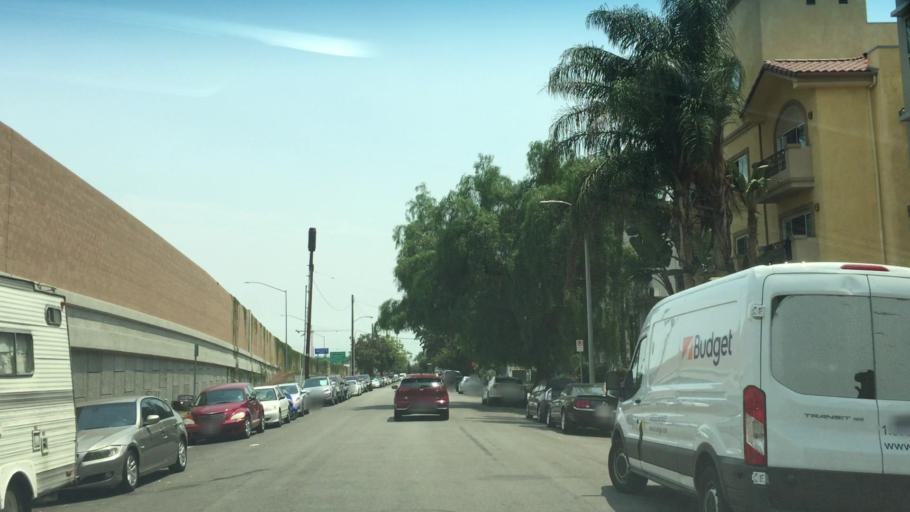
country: US
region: California
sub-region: Los Angeles County
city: Westwood, Los Angeles
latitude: 34.0452
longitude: -118.4460
